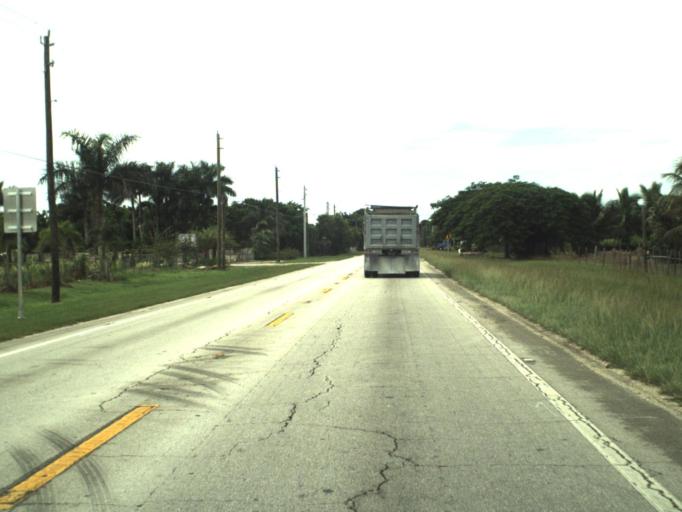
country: US
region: Florida
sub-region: Miami-Dade County
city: Naranja
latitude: 25.5483
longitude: -80.4781
